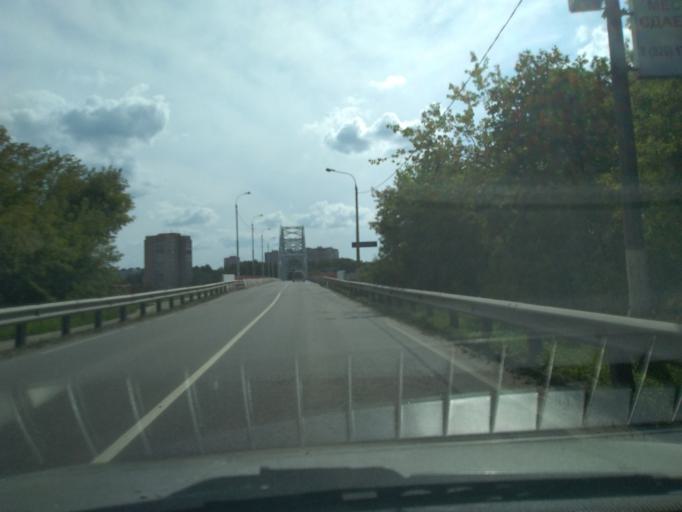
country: RU
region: Moskovskaya
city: Voskresensk
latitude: 55.3230
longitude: 38.6531
